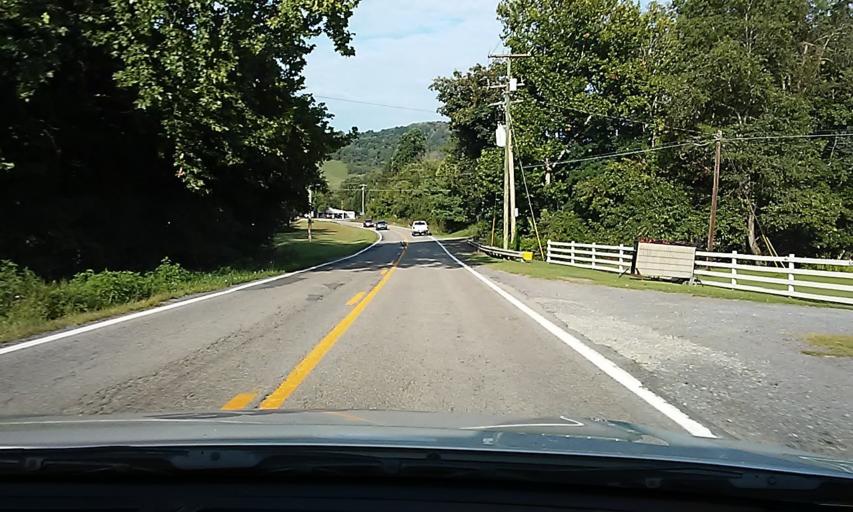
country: US
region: Pennsylvania
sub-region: Greene County
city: Morrisville
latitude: 39.7078
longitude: -80.1701
